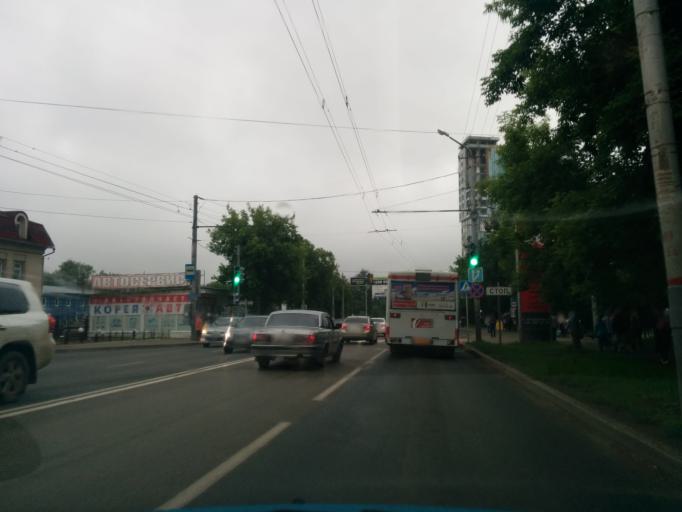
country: RU
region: Perm
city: Perm
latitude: 57.9969
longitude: 56.2226
